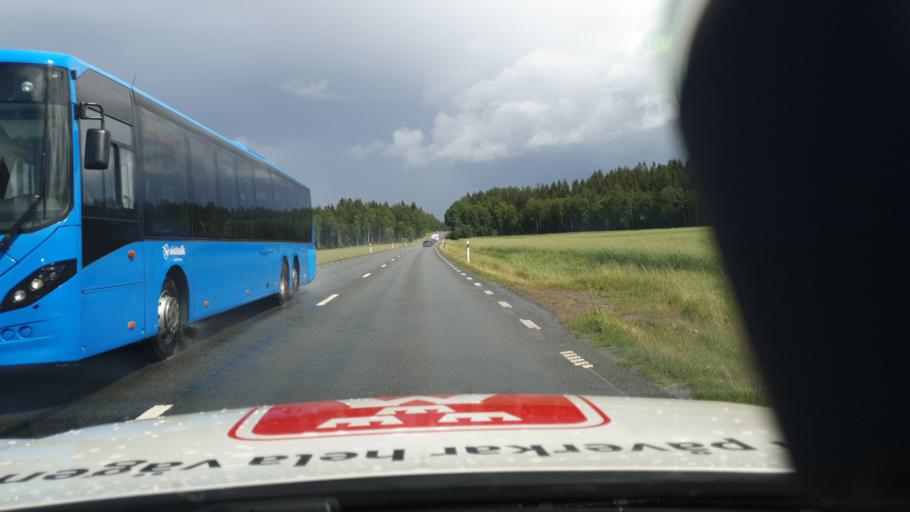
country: SE
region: Vaestra Goetaland
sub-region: Tidaholms Kommun
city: Tidaholm
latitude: 58.1343
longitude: 13.8779
